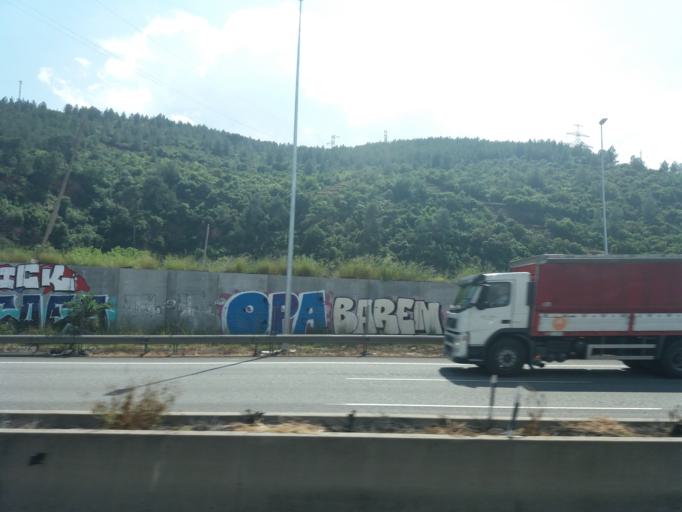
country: ES
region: Catalonia
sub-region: Provincia de Barcelona
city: Palleja
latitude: 41.4397
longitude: 1.9888
